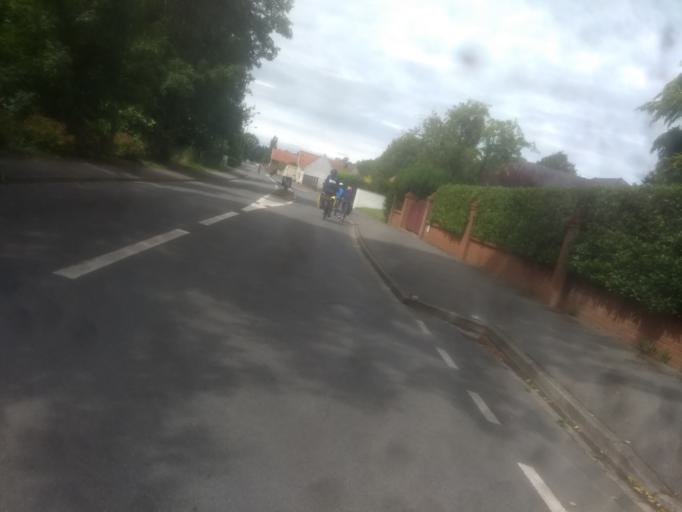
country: FR
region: Nord-Pas-de-Calais
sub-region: Departement du Pas-de-Calais
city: Anzin-Saint-Aubin
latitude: 50.3134
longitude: 2.7284
